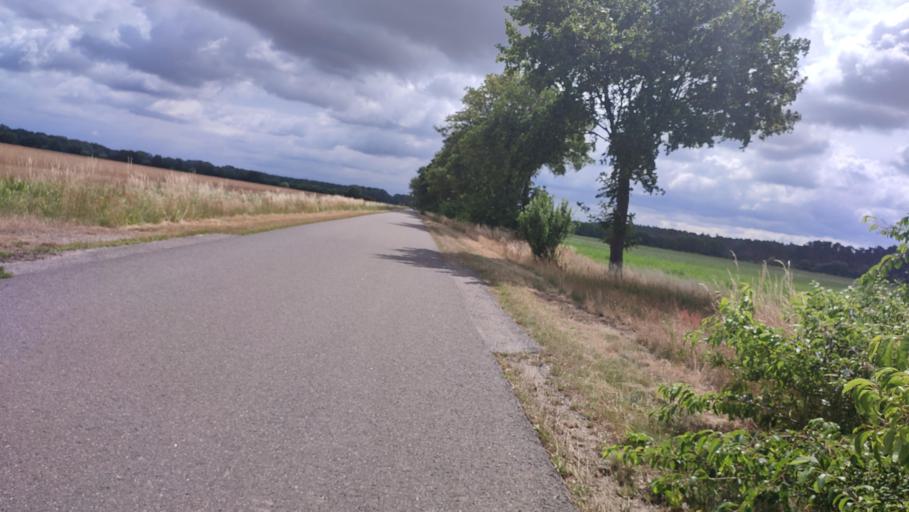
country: DE
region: Lower Saxony
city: Hitzacker
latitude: 53.1991
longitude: 11.1034
